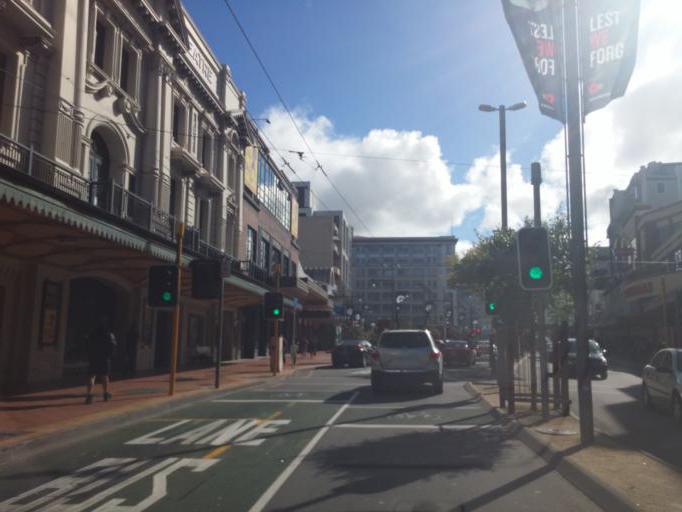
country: NZ
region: Wellington
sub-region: Wellington City
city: Wellington
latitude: -41.2930
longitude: 174.7802
